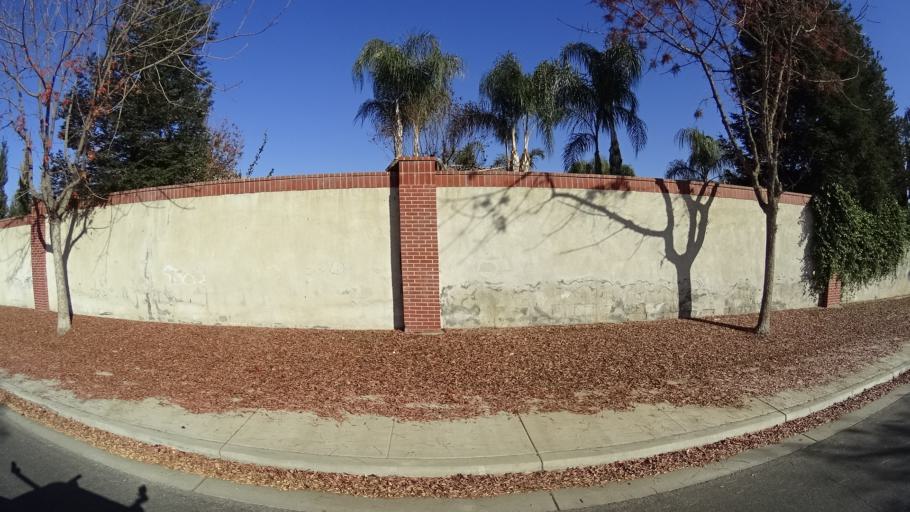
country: US
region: California
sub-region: Kern County
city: Rosedale
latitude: 35.3309
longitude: -119.1424
